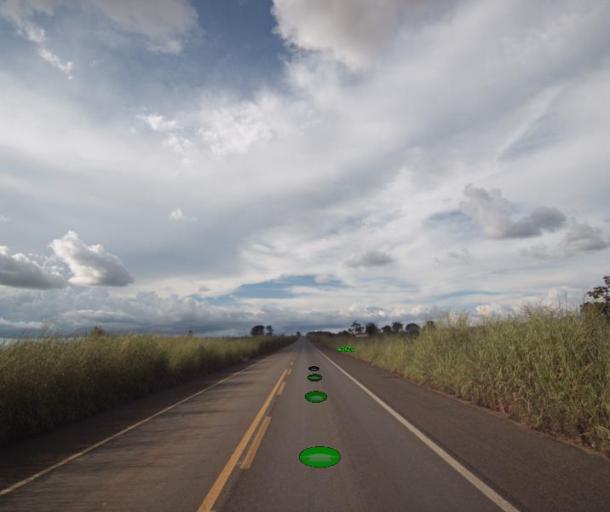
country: BR
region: Goias
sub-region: Niquelandia
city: Niquelandia
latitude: -14.7602
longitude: -48.6223
